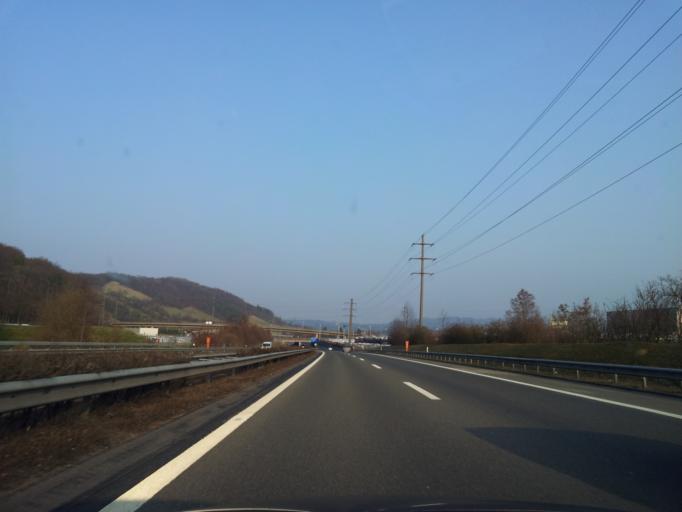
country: CH
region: Aargau
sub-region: Bezirk Brugg
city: Hausen
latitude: 47.4509
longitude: 8.2069
